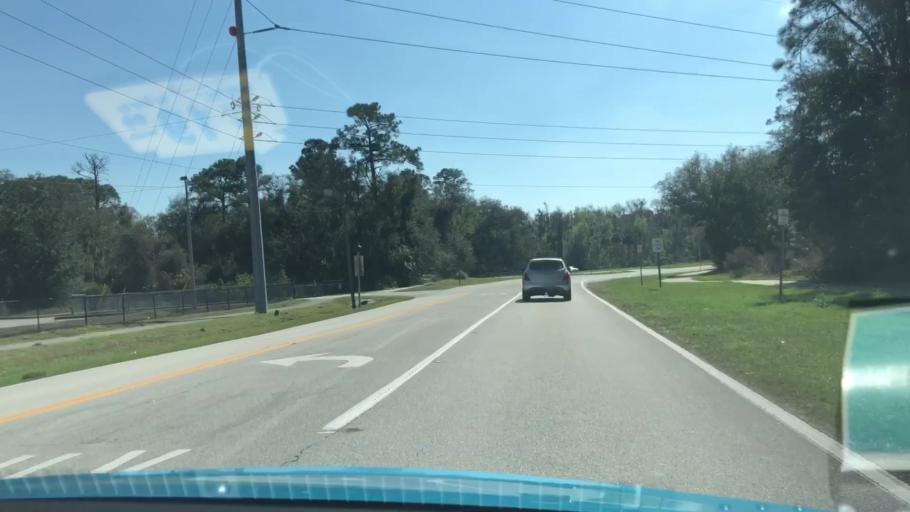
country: US
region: Florida
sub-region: Volusia County
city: Deltona
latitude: 28.8762
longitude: -81.2717
